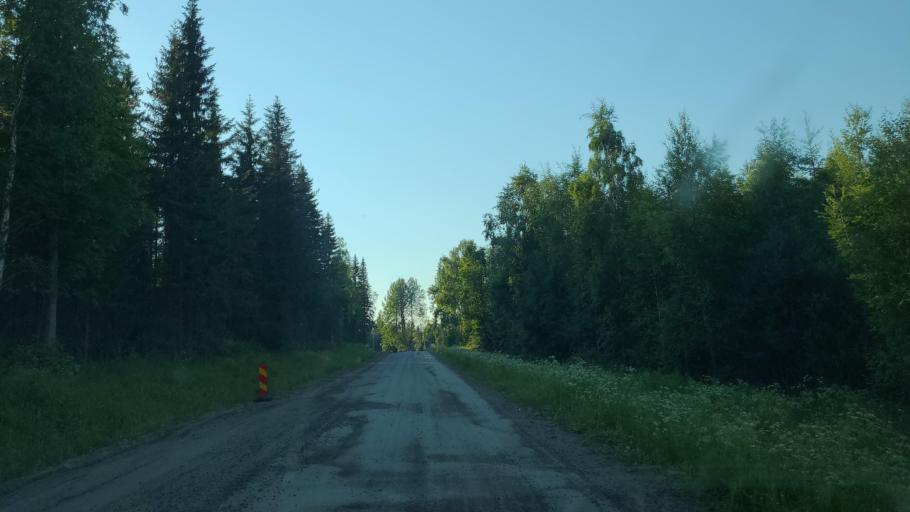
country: SE
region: Vaesterbotten
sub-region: Skelleftea Kommun
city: Burea
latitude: 64.4086
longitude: 21.3580
